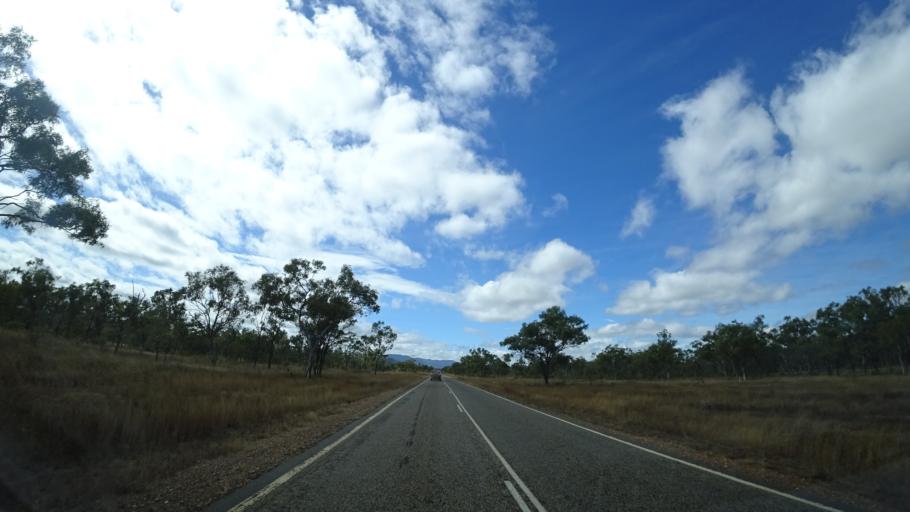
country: AU
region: Queensland
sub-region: Cairns
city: Port Douglas
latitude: -16.4973
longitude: 144.9807
